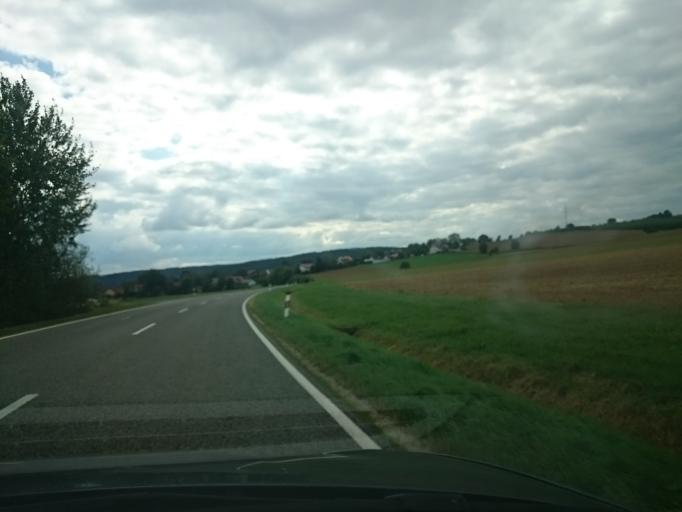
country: DE
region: Bavaria
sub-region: Regierungsbezirk Mittelfranken
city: Thalmassing
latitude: 49.1297
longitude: 11.2696
